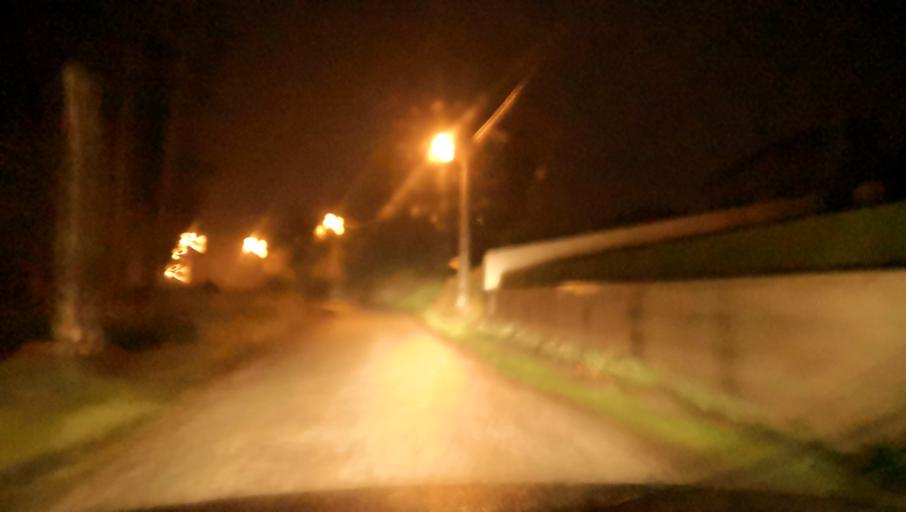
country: PT
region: Vila Real
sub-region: Vila Real
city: Vila Real
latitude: 41.3369
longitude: -7.7224
